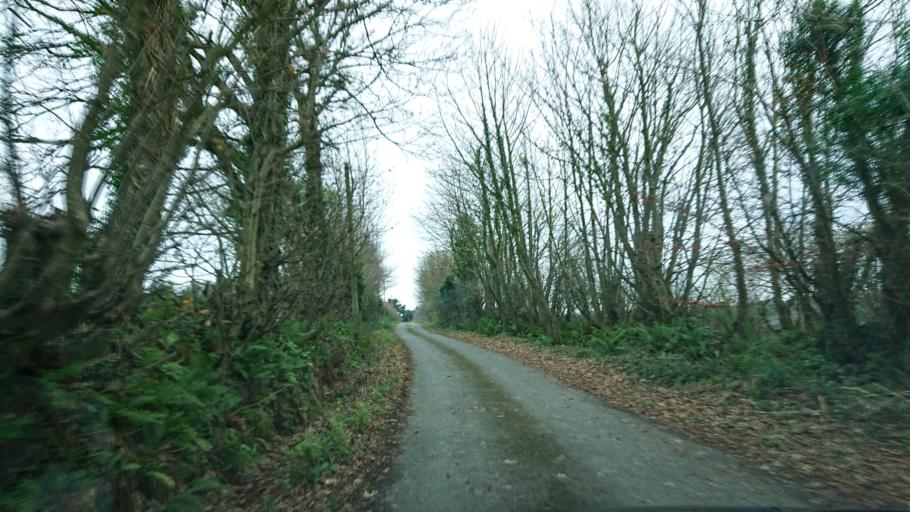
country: IE
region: Munster
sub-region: Waterford
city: Dunmore East
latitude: 52.1945
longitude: -7.0348
